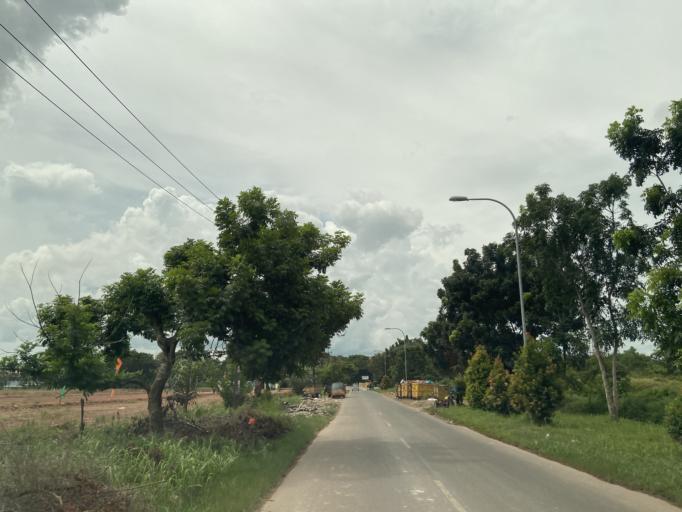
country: SG
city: Singapore
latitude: 1.0431
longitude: 103.9694
